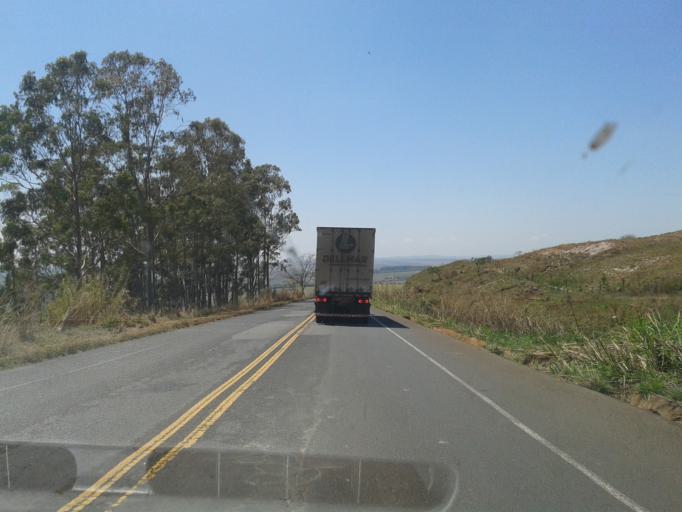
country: BR
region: Minas Gerais
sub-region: Araxa
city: Araxa
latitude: -19.4239
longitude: -47.2393
